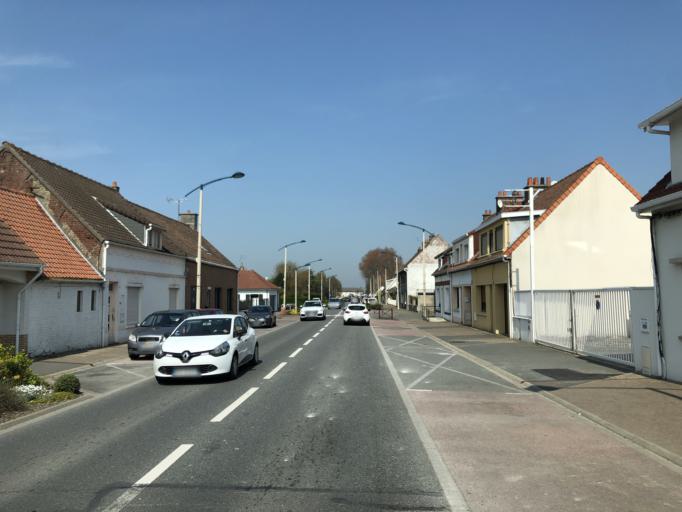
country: FR
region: Nord-Pas-de-Calais
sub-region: Departement du Pas-de-Calais
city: Coquelles
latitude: 50.9372
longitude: 1.8011
